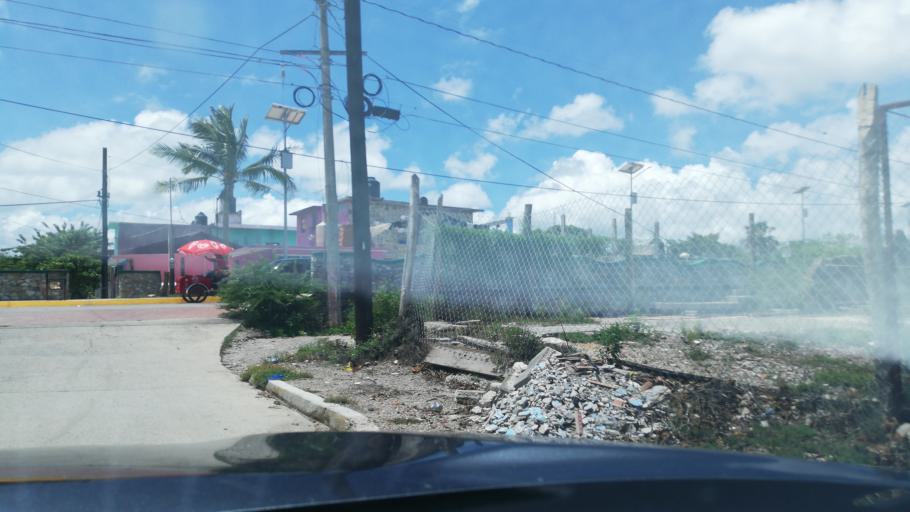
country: MX
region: Oaxaca
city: Asuncion Ixtaltepec
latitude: 16.5037
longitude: -95.0556
